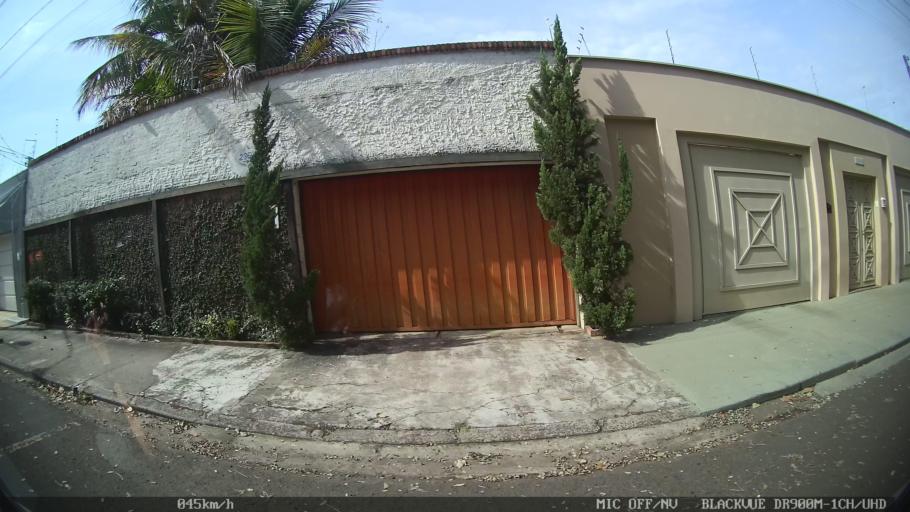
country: BR
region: Sao Paulo
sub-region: Piracicaba
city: Piracicaba
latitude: -22.7125
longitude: -47.6759
